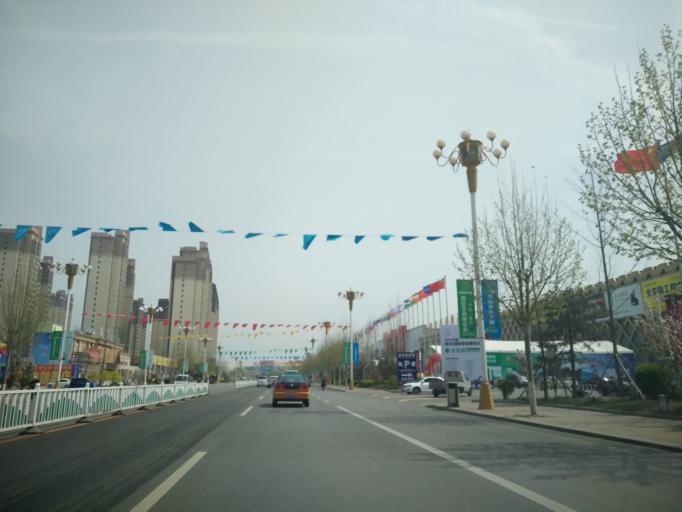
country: CN
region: Beijing
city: Xiji
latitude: 39.7465
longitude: 116.9935
